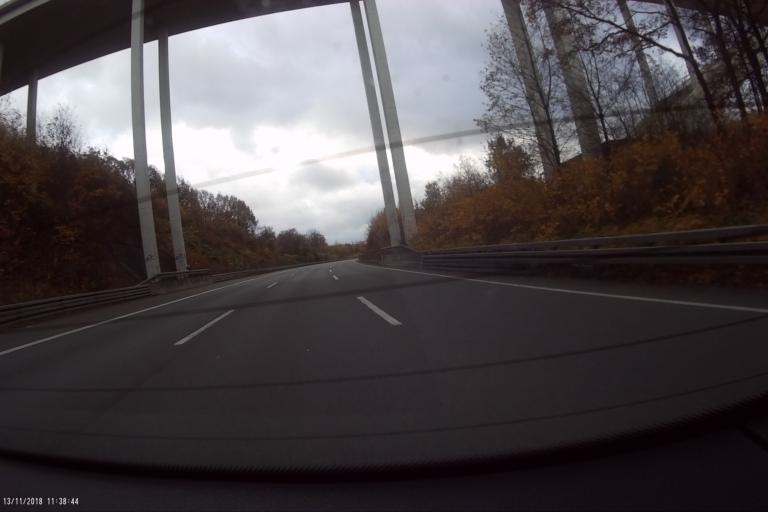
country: DE
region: North Rhine-Westphalia
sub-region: Regierungsbezirk Dusseldorf
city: Wuppertal
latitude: 51.2399
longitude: 7.2309
